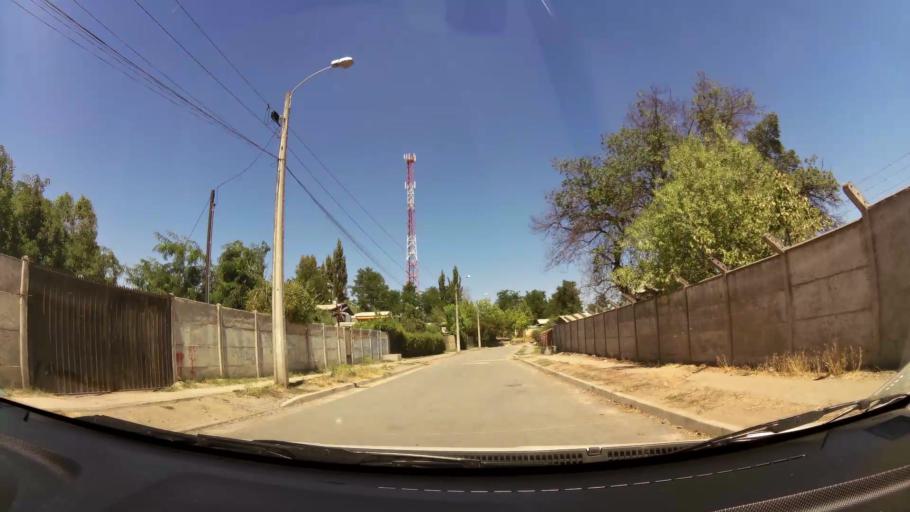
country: CL
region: O'Higgins
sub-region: Provincia de Cachapoal
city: Rancagua
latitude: -34.2250
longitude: -70.7873
